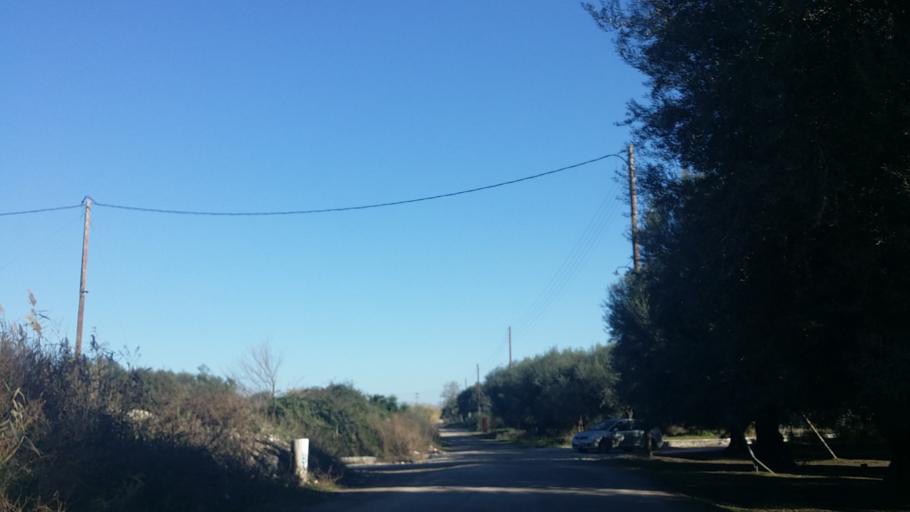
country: GR
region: West Greece
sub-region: Nomos Achaias
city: Temeni
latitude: 38.1948
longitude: 22.1826
